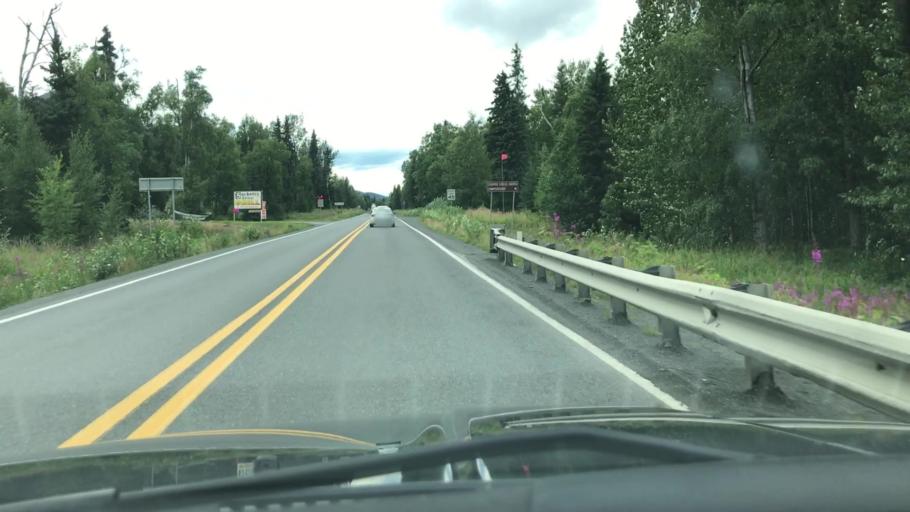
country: US
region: Alaska
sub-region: Kenai Peninsula Borough
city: Seward
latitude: 60.4839
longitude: -149.8832
